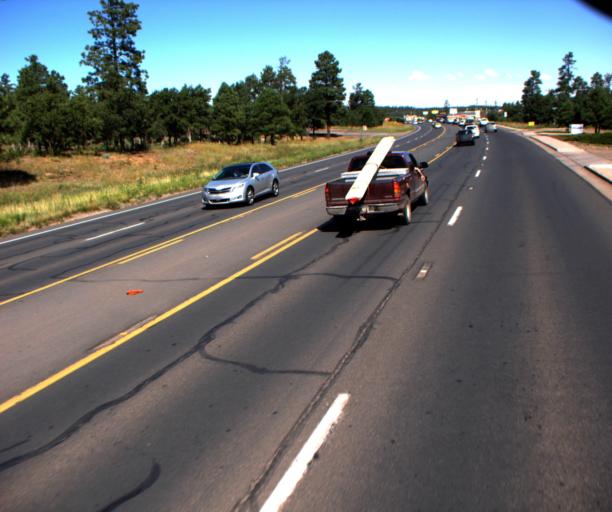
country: US
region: Arizona
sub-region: Navajo County
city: Show Low
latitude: 34.2057
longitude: -110.0208
